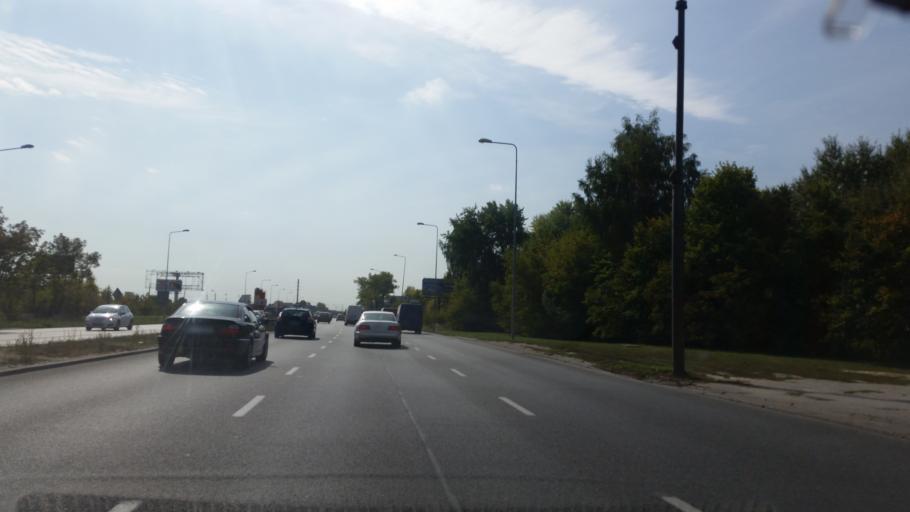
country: PL
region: Masovian Voivodeship
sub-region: Powiat piaseczynski
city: Mysiadlo
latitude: 52.1044
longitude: 21.0185
